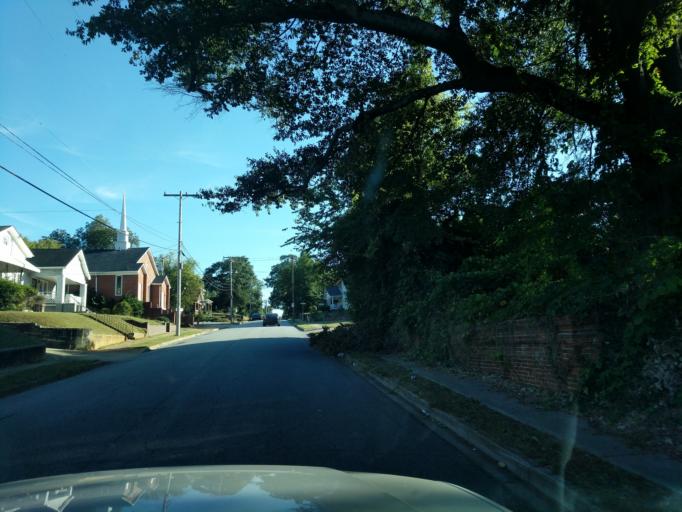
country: US
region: South Carolina
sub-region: Spartanburg County
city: Spartanburg
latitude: 34.9573
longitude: -81.9267
